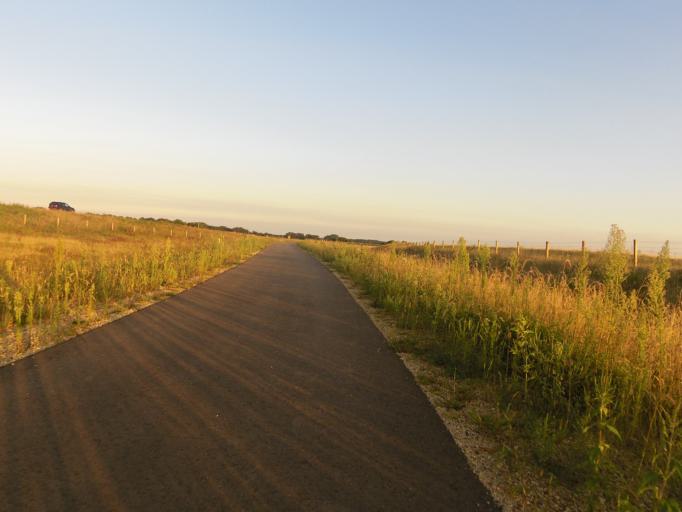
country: US
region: Minnesota
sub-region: Washington County
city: Stillwater
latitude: 45.0588
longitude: -92.7830
